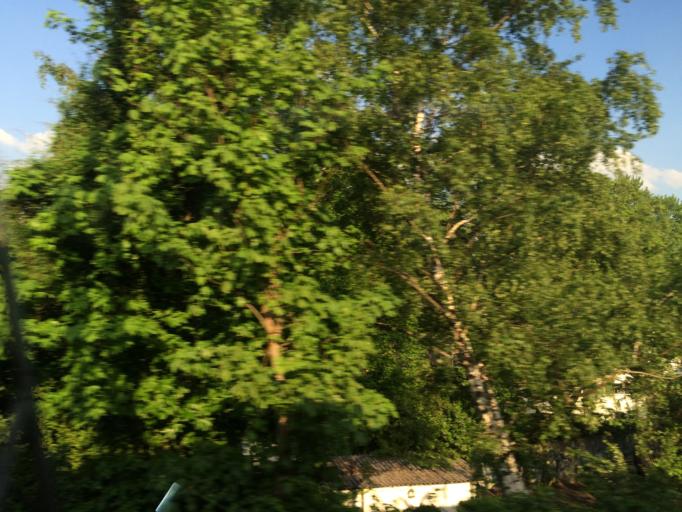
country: DE
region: North Rhine-Westphalia
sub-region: Regierungsbezirk Dusseldorf
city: Duisburg
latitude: 51.4176
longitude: 6.7752
